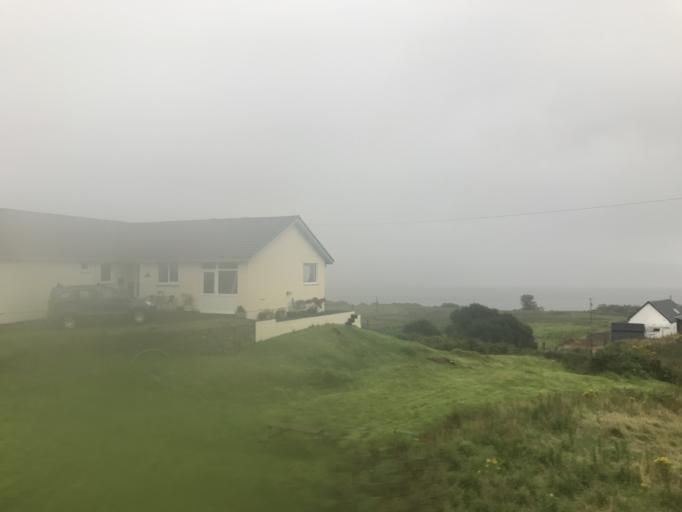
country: GB
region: Scotland
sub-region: Argyll and Bute
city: Isle Of Mull
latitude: 56.5631
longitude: -5.9907
